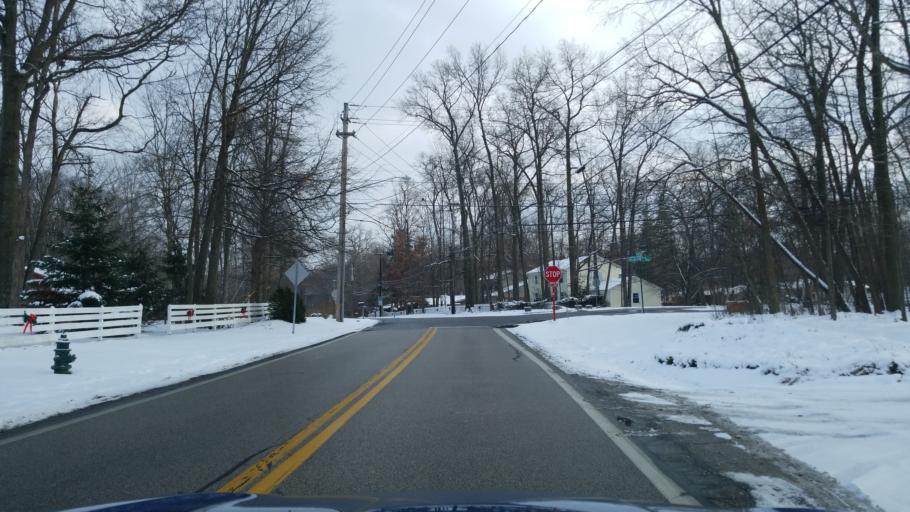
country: US
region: Ohio
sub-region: Cuyahoga County
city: Strongsville
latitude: 41.3341
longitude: -81.8450
